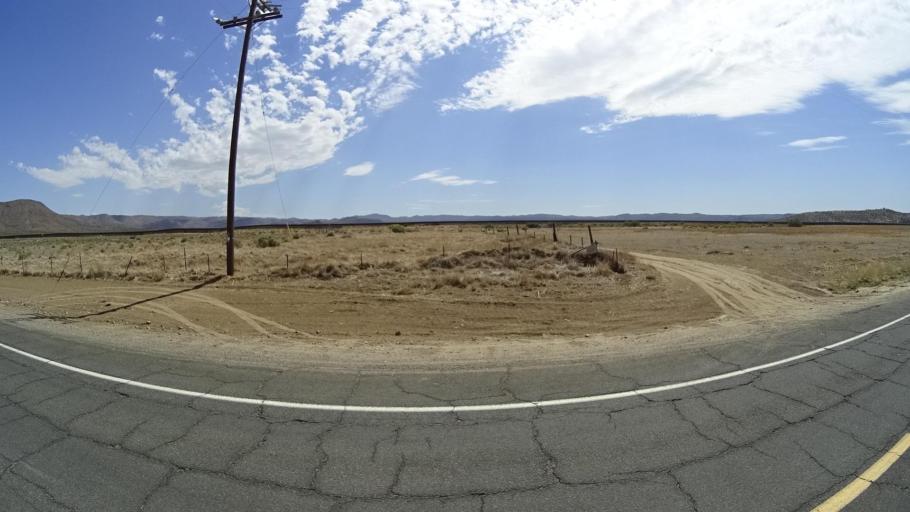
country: MX
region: Baja California
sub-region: Tecate
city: Cereso del Hongo
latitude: 32.6176
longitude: -116.1700
